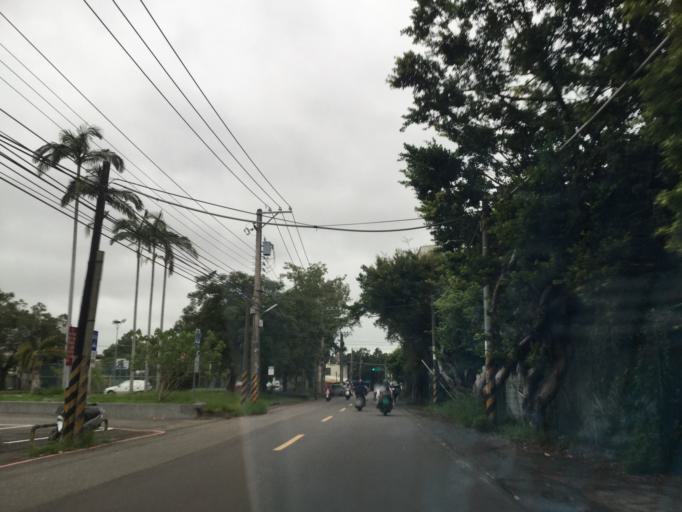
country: TW
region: Taiwan
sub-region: Hsinchu
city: Hsinchu
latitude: 24.7948
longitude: 121.0030
